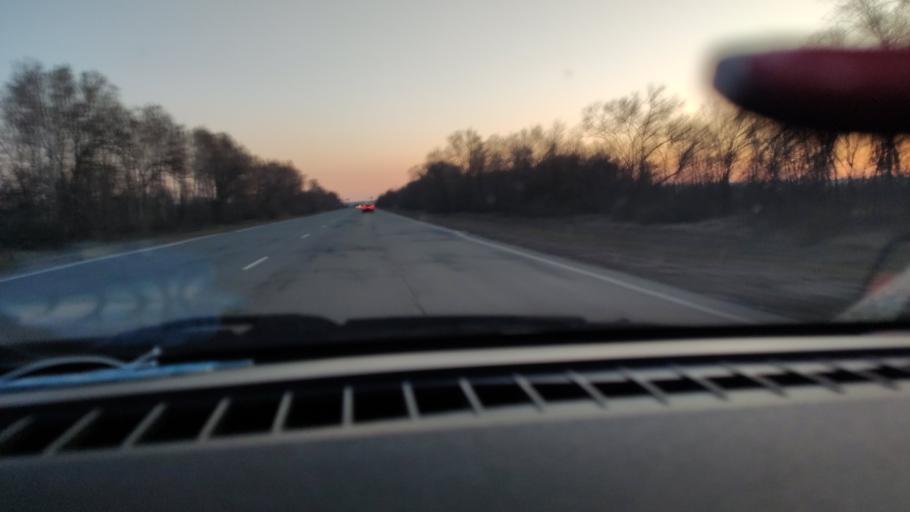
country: RU
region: Saratov
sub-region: Saratovskiy Rayon
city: Saratov
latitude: 51.6992
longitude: 46.0103
